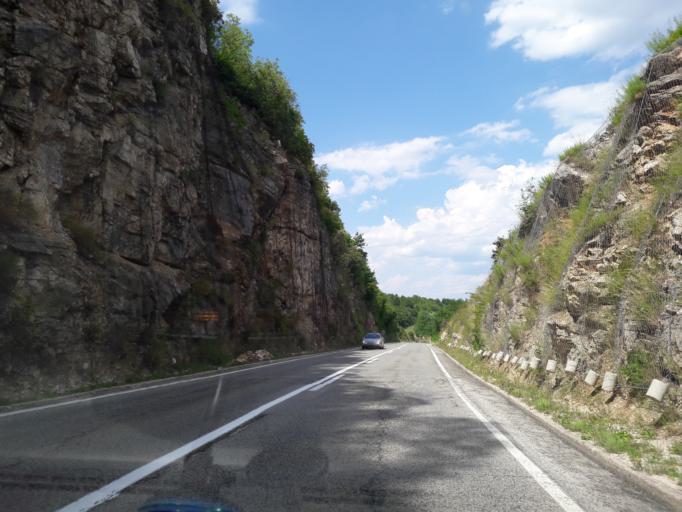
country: BA
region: Republika Srpska
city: Mrkonjic Grad
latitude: 44.5019
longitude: 17.1496
